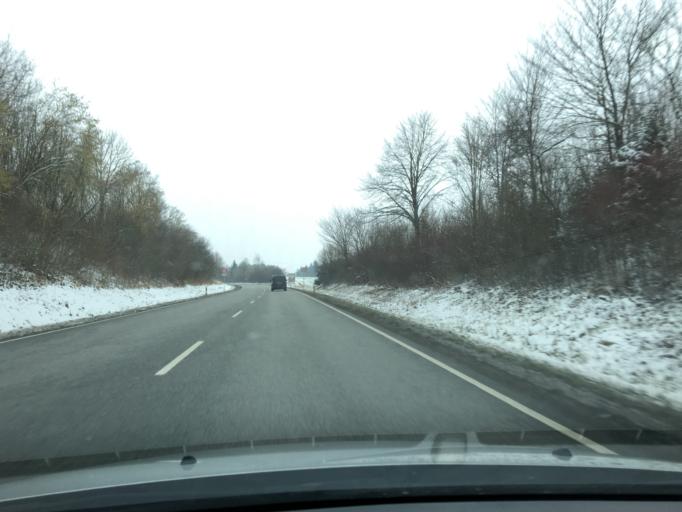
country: DE
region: Bavaria
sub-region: Lower Bavaria
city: Furth
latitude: 48.4277
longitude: 12.3983
